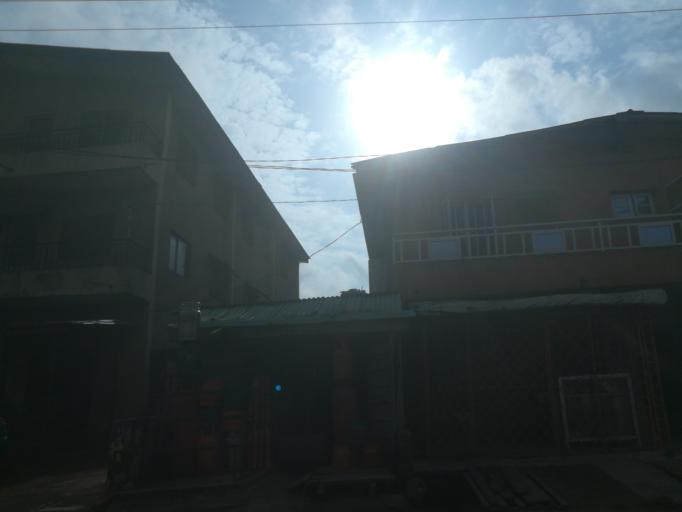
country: NG
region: Lagos
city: Agege
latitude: 6.6208
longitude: 3.3128
